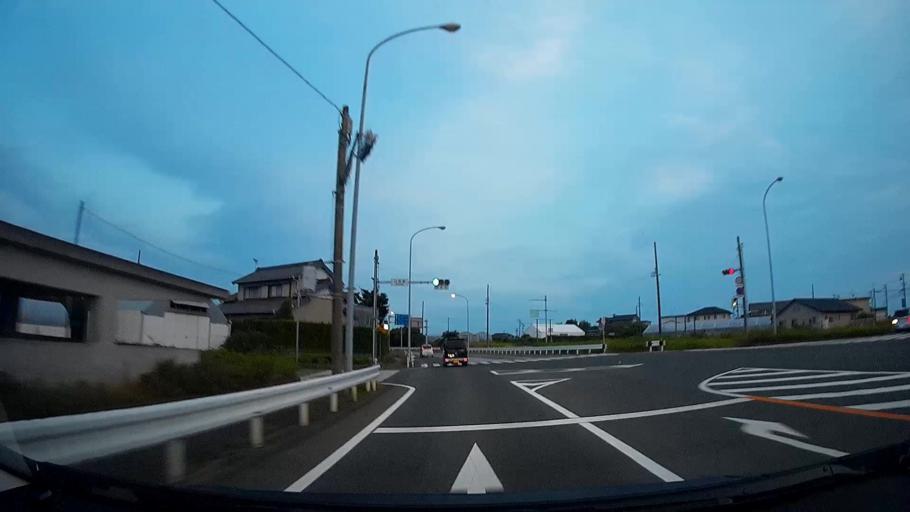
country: JP
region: Shizuoka
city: Kosai-shi
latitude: 34.6872
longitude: 137.4992
